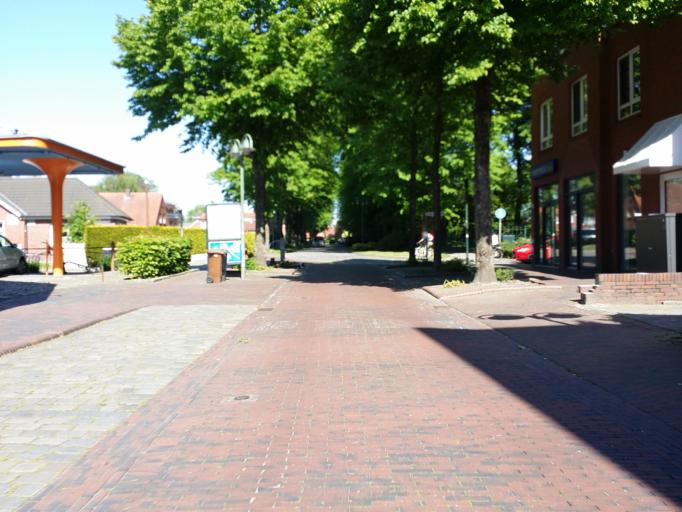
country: DE
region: Lower Saxony
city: Esens
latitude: 53.6473
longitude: 7.6148
